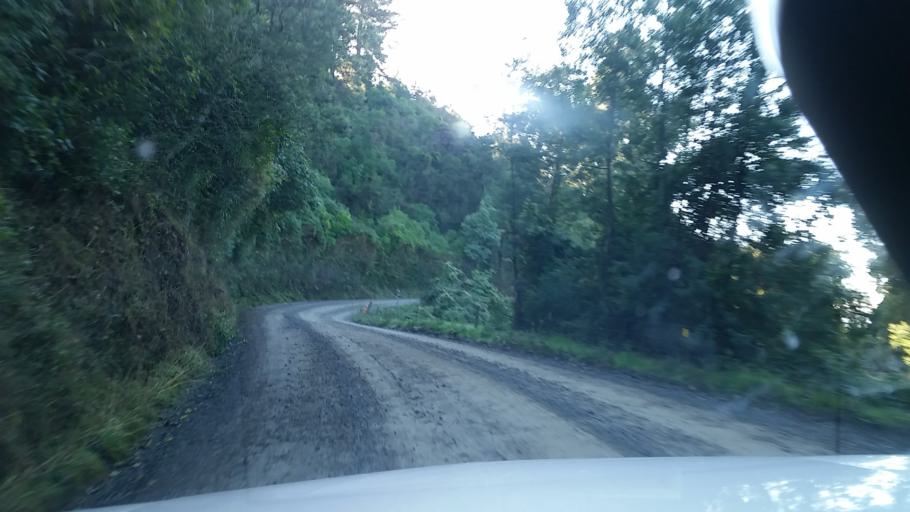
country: NZ
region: Marlborough
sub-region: Marlborough District
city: Blenheim
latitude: -41.4465
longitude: 173.8805
